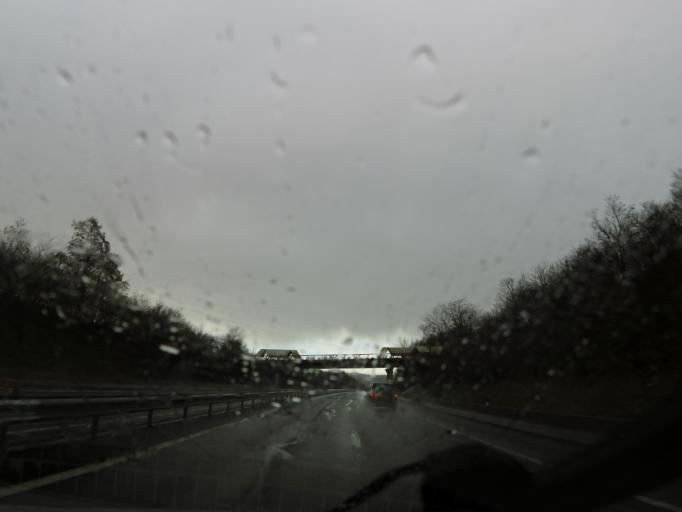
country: FR
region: Bourgogne
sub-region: Departement de Saone-et-Loire
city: Sance
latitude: 46.3415
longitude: 4.8390
